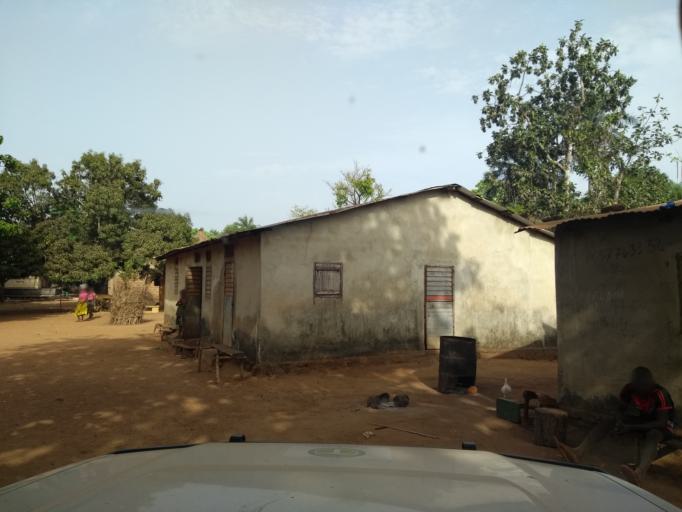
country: GN
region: Kindia
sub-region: Prefecture de Dubreka
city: Dubreka
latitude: 9.8144
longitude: -13.5606
